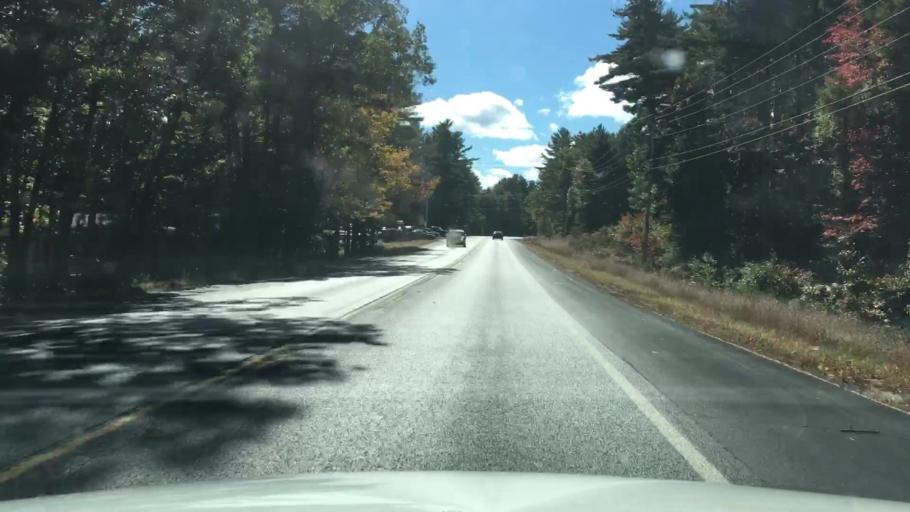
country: US
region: Maine
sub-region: York County
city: Alfred
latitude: 43.4540
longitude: -70.7226
